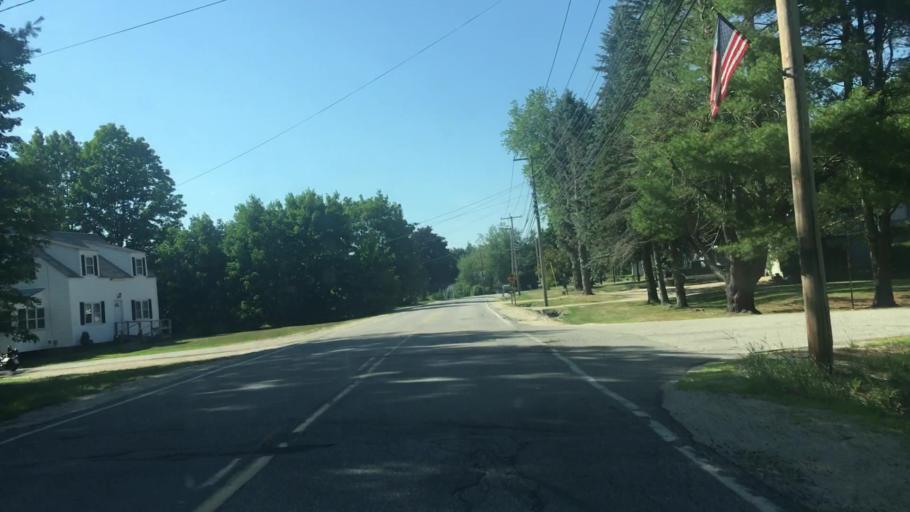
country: US
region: Maine
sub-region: York County
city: Buxton
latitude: 43.6093
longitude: -70.5394
